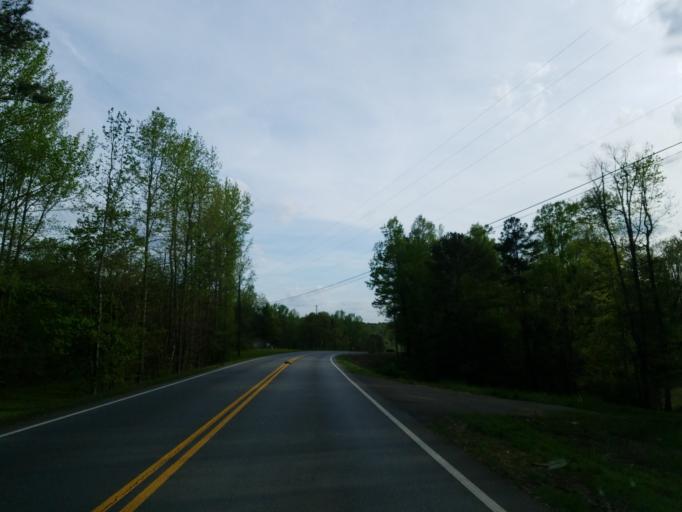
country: US
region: Georgia
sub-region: Cherokee County
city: Ball Ground
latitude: 34.2744
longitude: -84.3009
